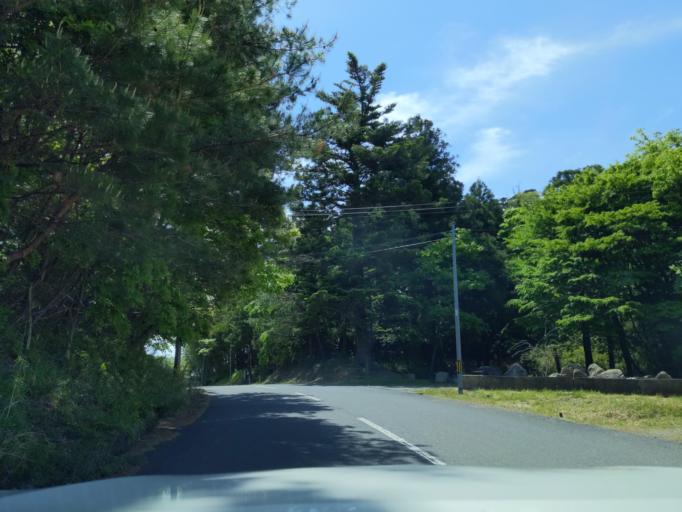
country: JP
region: Fukushima
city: Koriyama
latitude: 37.4169
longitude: 140.2973
